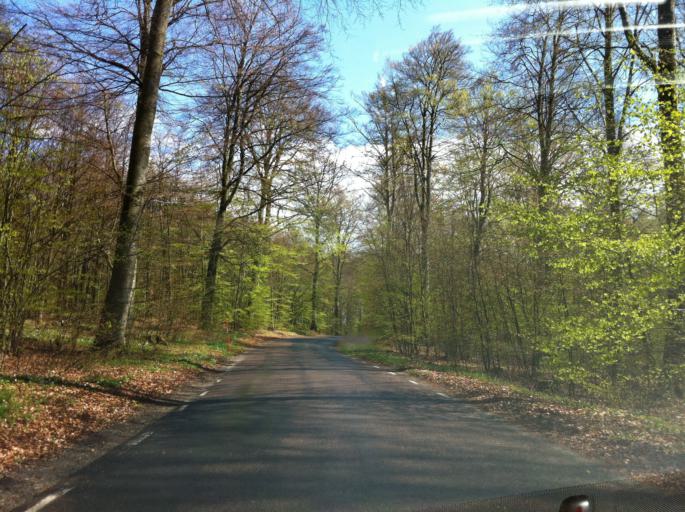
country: SE
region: Skane
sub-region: Horby Kommun
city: Hoerby
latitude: 55.8795
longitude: 13.6419
